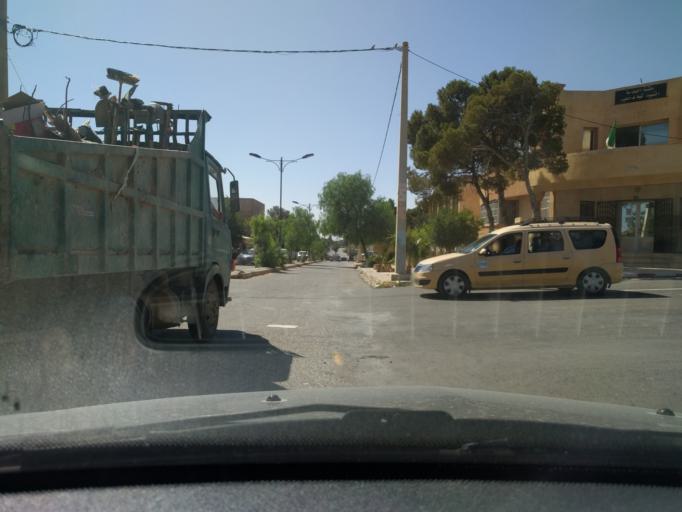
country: DZ
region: Tiaret
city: Frenda
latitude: 34.8949
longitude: 1.2422
